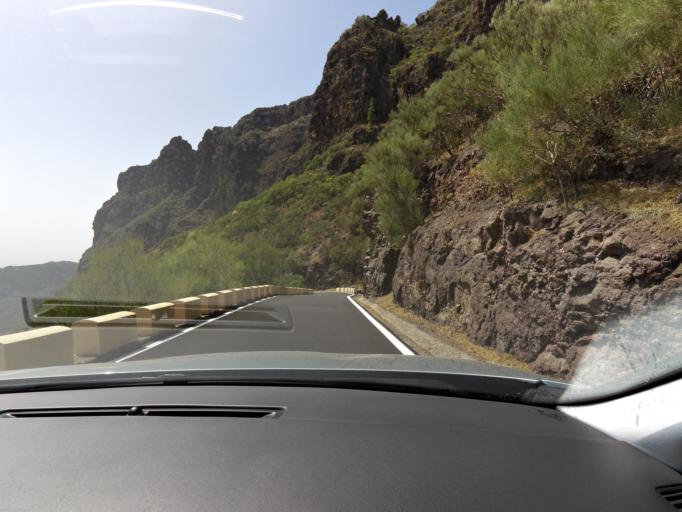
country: ES
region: Canary Islands
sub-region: Provincia de Santa Cruz de Tenerife
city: Santiago del Teide
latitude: 28.3032
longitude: -16.8285
